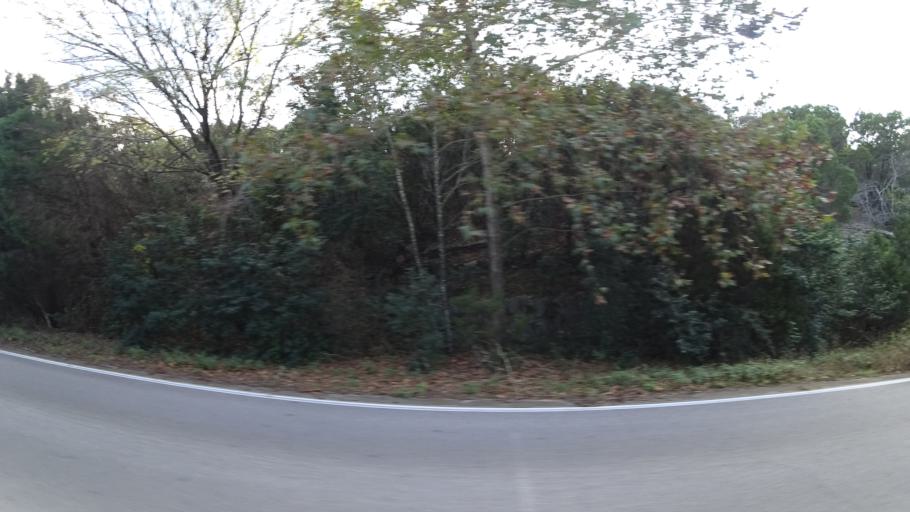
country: US
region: Texas
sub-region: Travis County
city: Barton Creek
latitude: 30.2716
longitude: -97.8533
